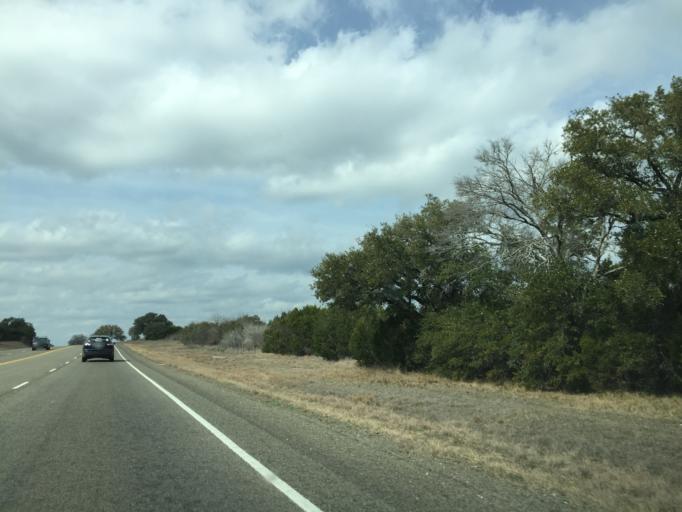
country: US
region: Texas
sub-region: Burnet County
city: Meadowlakes
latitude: 30.5027
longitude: -98.2728
